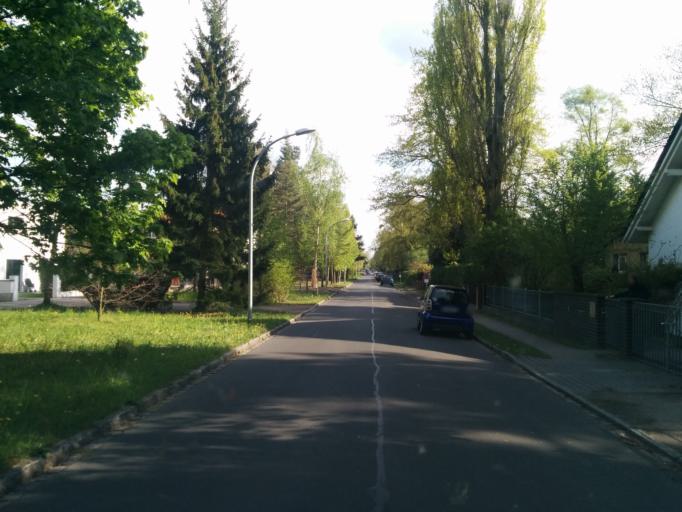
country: DE
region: Brandenburg
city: Kleinmachnow
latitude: 52.4092
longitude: 13.2045
